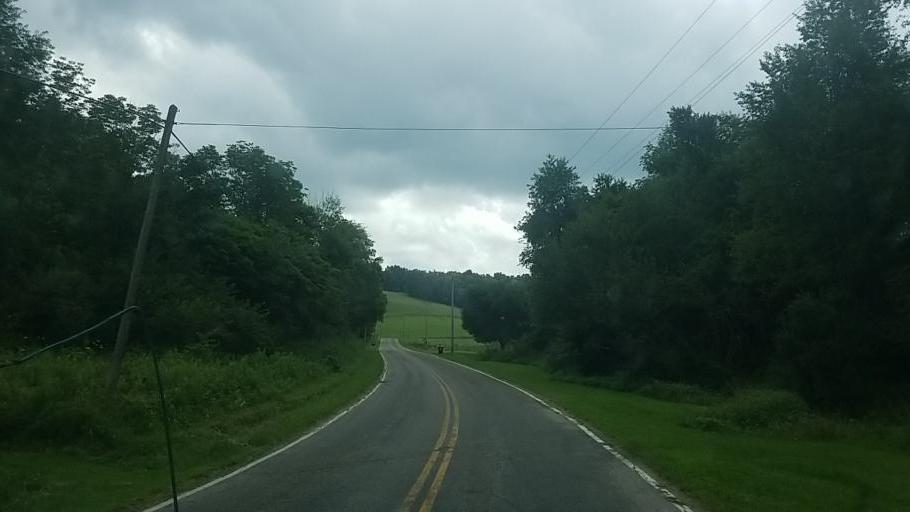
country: US
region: Ohio
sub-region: Muskingum County
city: Frazeysburg
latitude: 40.1560
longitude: -82.2570
